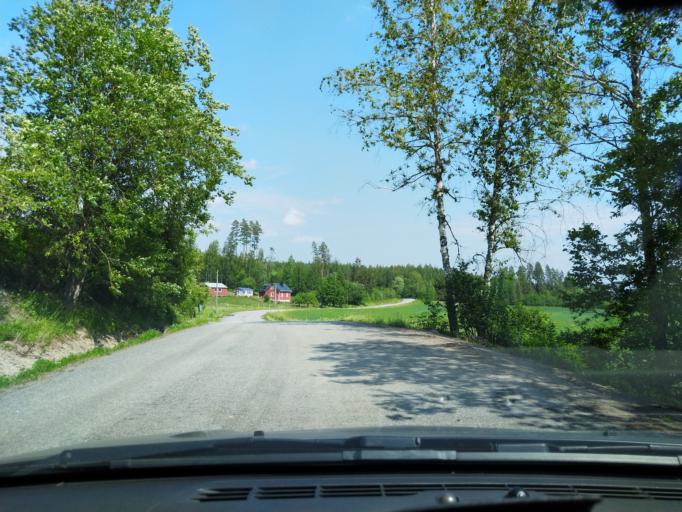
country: FI
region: Uusimaa
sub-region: Helsinki
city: Lohja
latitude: 60.3408
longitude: 24.0725
